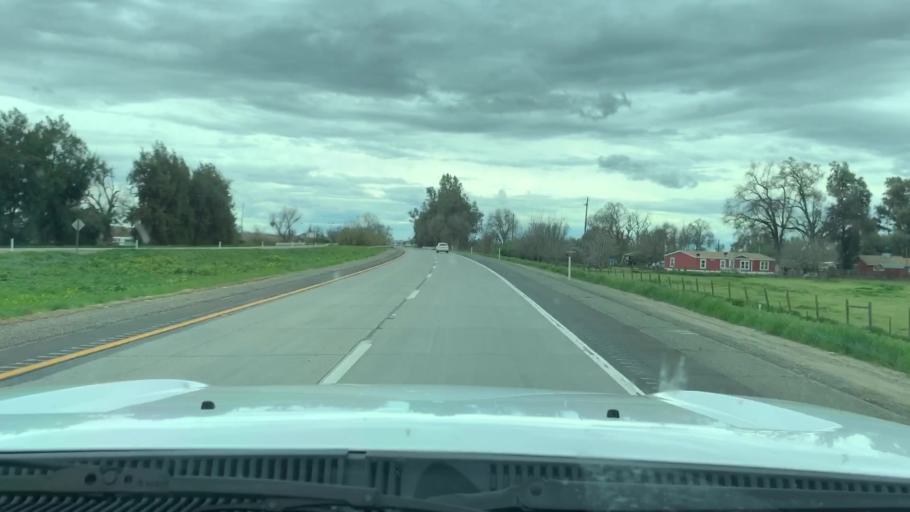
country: US
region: California
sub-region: Kings County
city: Lemoore
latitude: 36.3650
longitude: -119.8103
